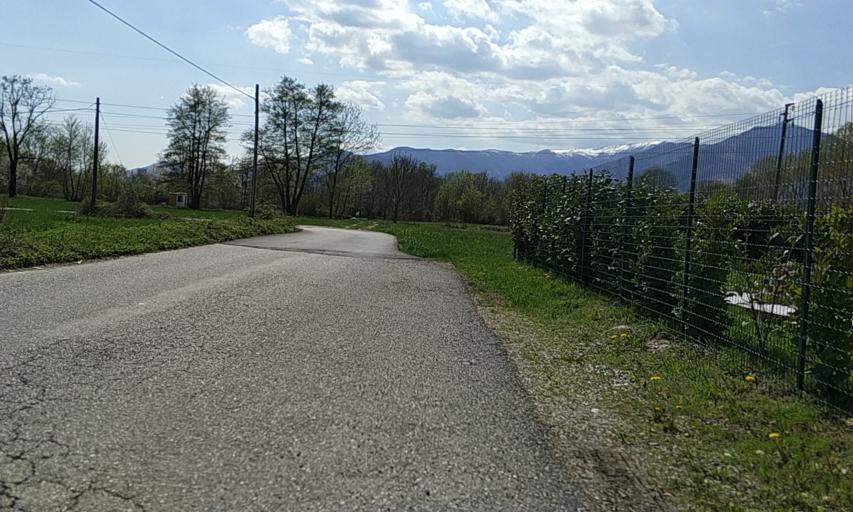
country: IT
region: Piedmont
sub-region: Provincia di Torino
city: Villanova Canavese
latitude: 45.2395
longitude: 7.5554
